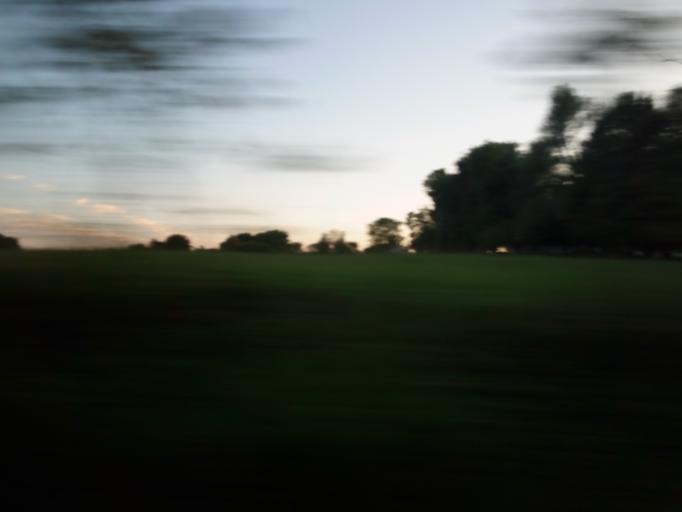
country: US
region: Kentucky
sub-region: Oldham County
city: Pewee Valley
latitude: 38.2843
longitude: -85.4881
